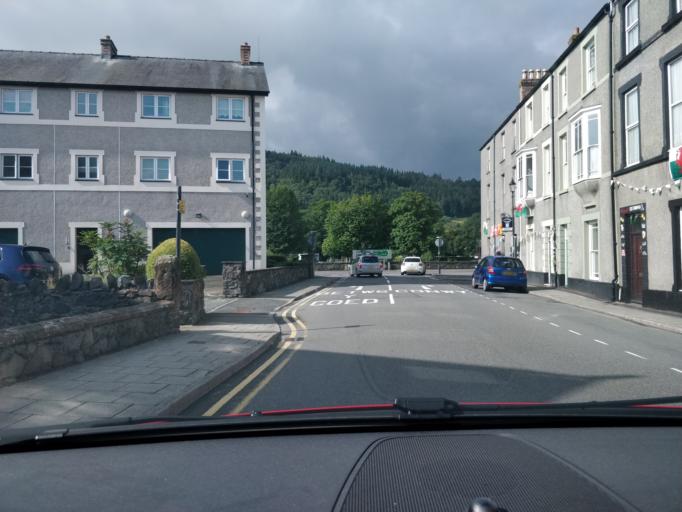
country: GB
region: Wales
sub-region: Conwy
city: Llanrwst
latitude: 53.1373
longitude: -3.7960
